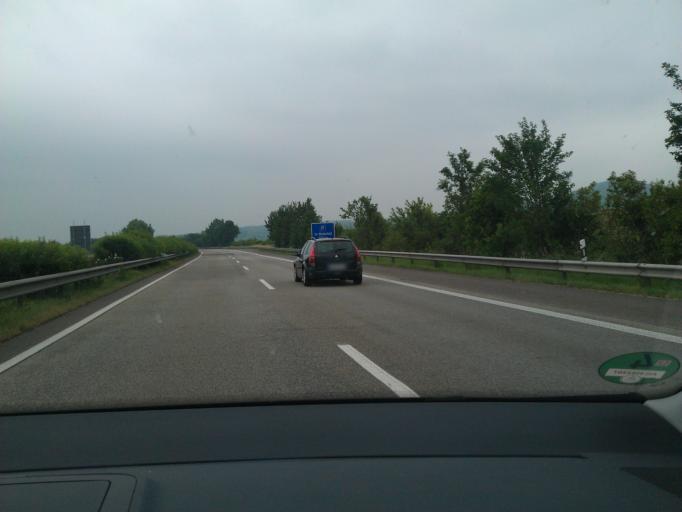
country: DE
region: Rheinland-Pfalz
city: Saffig
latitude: 50.3699
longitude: 7.4188
